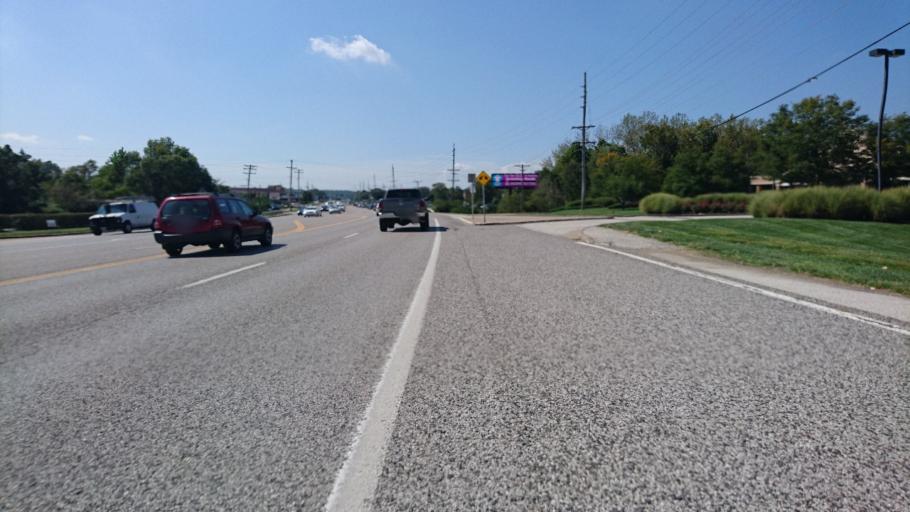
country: US
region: Missouri
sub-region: Saint Louis County
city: Manchester
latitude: 38.5967
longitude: -90.4865
